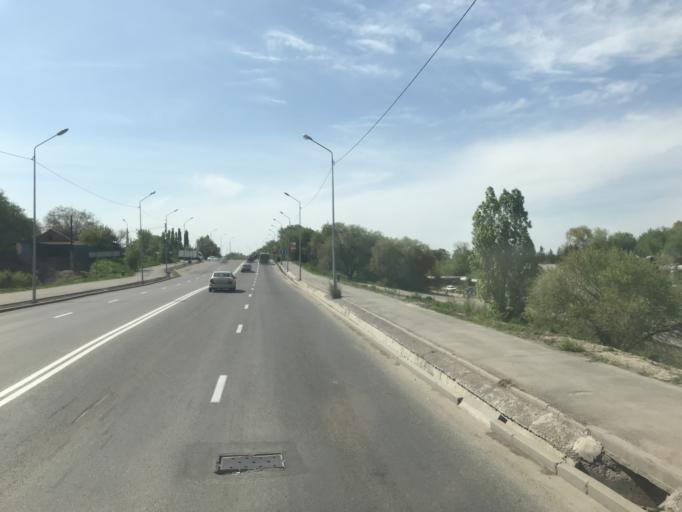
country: KZ
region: Almaty Oblysy
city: Burunday
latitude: 43.3105
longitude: 76.8684
